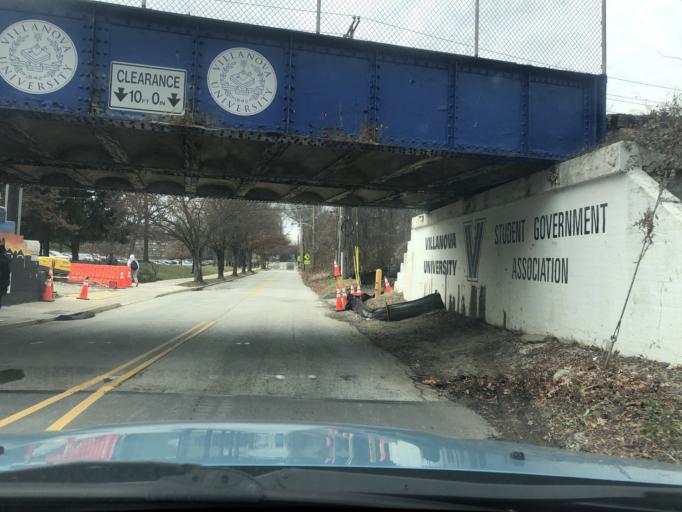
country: US
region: Pennsylvania
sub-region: Delaware County
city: Radnor
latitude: 40.0331
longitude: -75.3408
